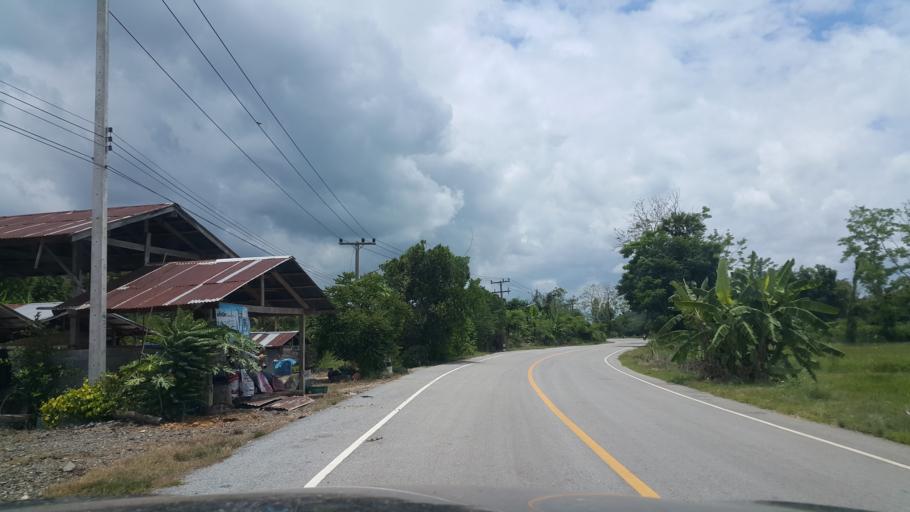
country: TH
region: Sukhothai
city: Kong Krailat
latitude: 16.9353
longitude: 99.9257
